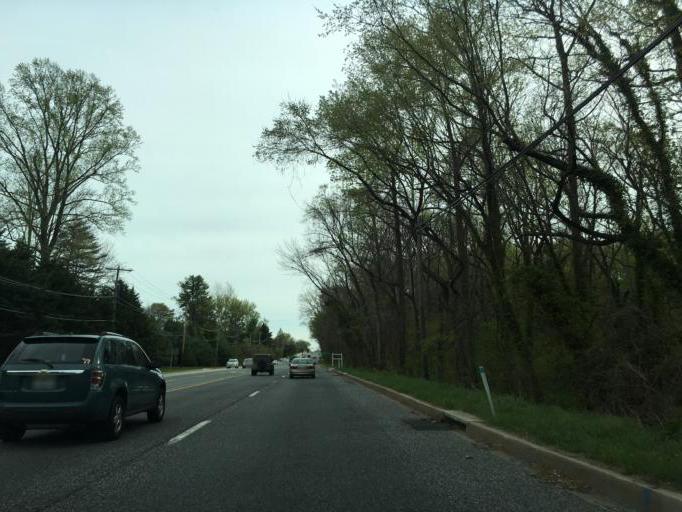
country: US
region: Maryland
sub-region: Baltimore County
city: Hampton
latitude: 39.4223
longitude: -76.5977
